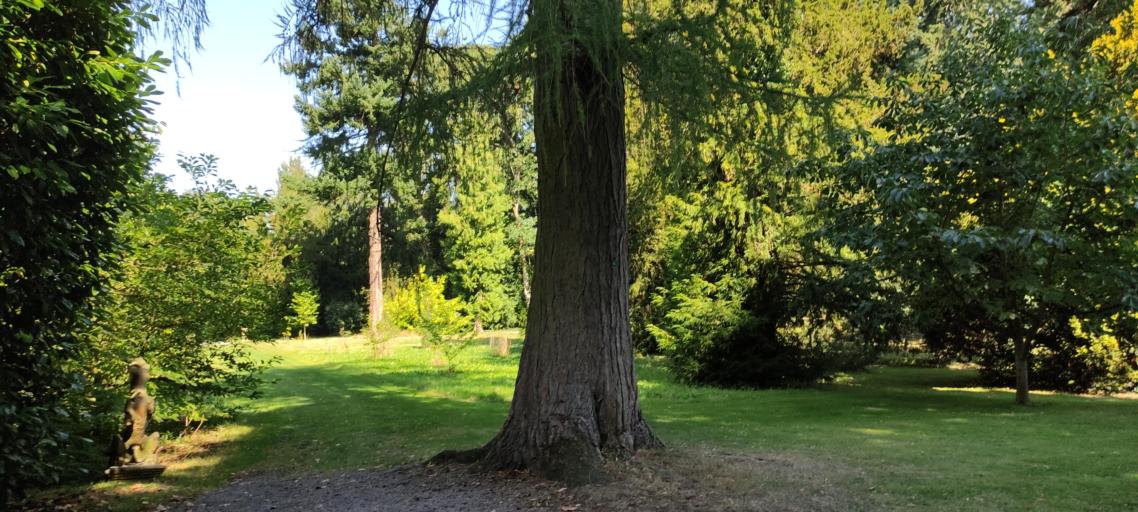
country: GB
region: England
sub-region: North Yorkshire
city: Bedale
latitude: 54.2648
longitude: -1.6000
